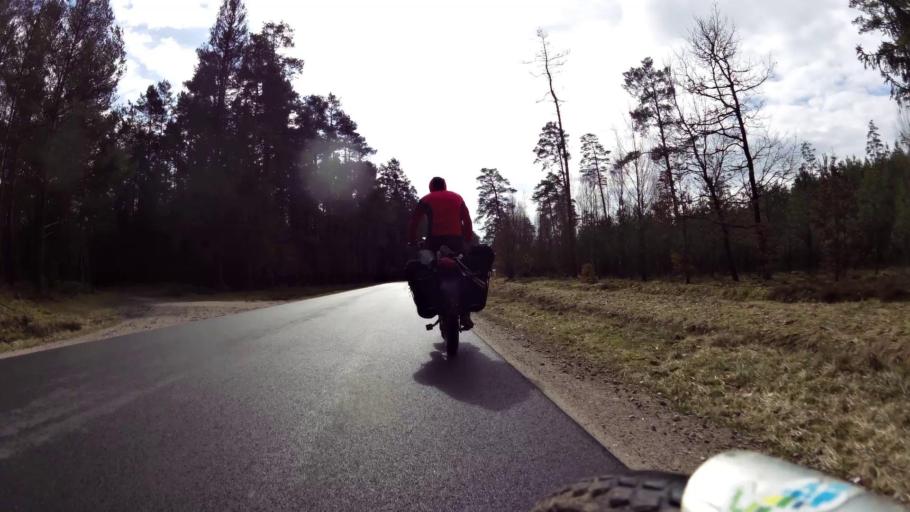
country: PL
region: Pomeranian Voivodeship
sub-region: Powiat bytowski
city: Kolczyglowy
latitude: 54.2033
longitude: 17.2353
